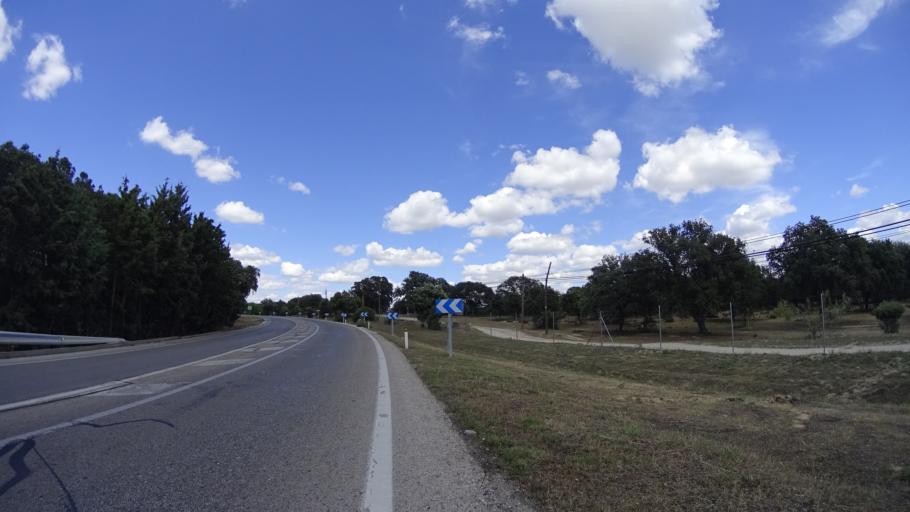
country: ES
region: Madrid
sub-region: Provincia de Madrid
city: Boadilla del Monte
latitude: 40.4274
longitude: -3.8698
